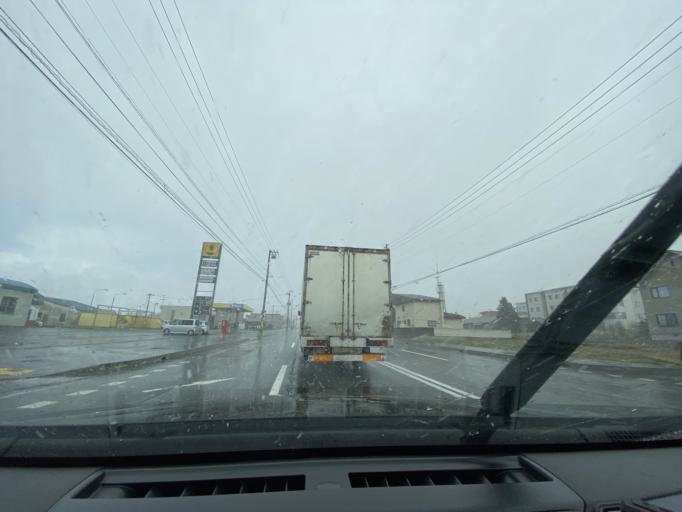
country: JP
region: Hokkaido
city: Takikawa
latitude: 43.6279
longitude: 141.9423
